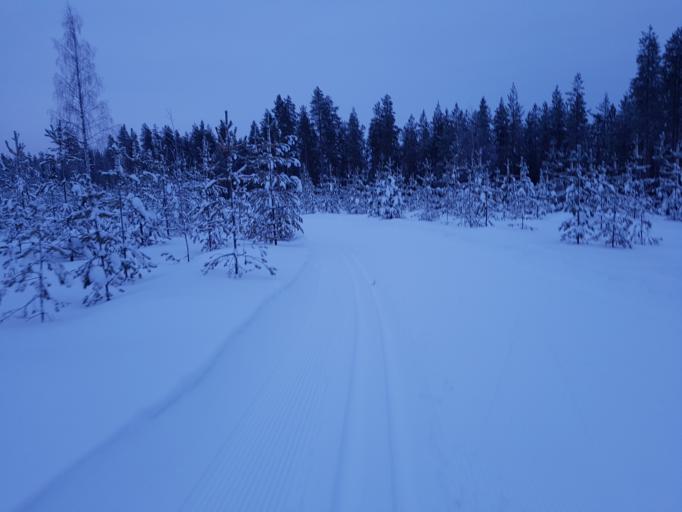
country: FI
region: Kainuu
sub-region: Kehys-Kainuu
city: Kuhmo
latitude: 64.0863
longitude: 29.5171
